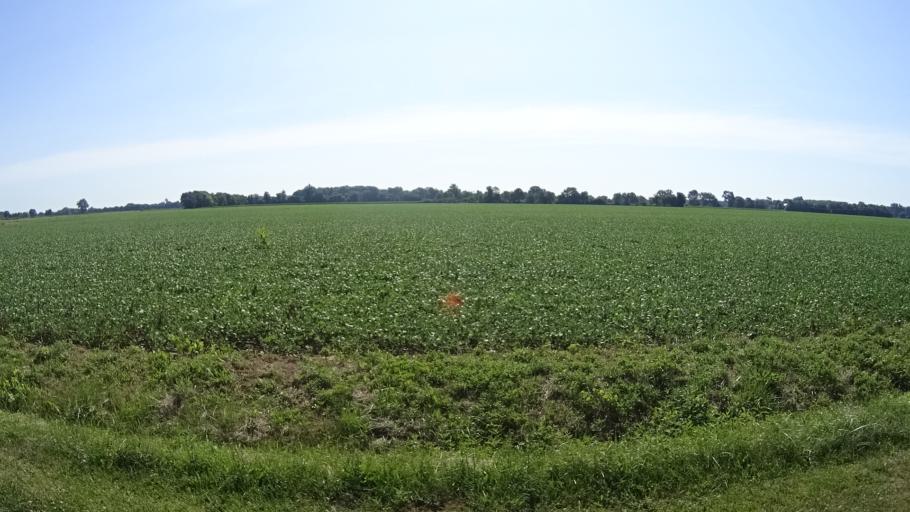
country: US
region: Ohio
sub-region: Huron County
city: Bellevue
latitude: 41.3656
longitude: -82.8189
